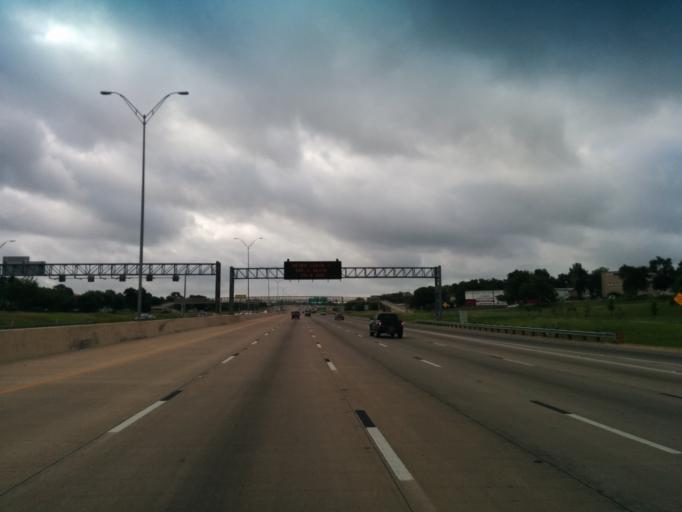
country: US
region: Texas
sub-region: Bexar County
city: Balcones Heights
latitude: 29.4797
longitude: -98.5237
